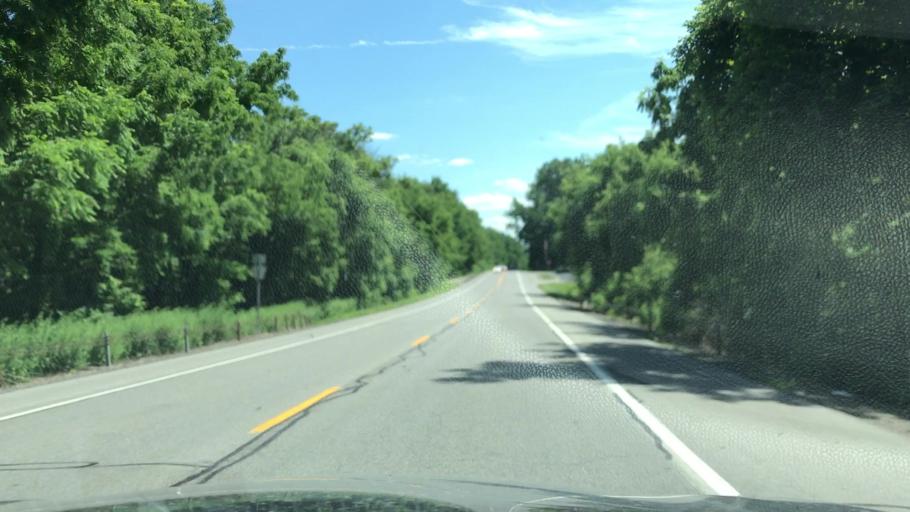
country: US
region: New York
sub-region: Livingston County
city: Mount Morris
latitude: 42.7546
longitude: -77.8842
